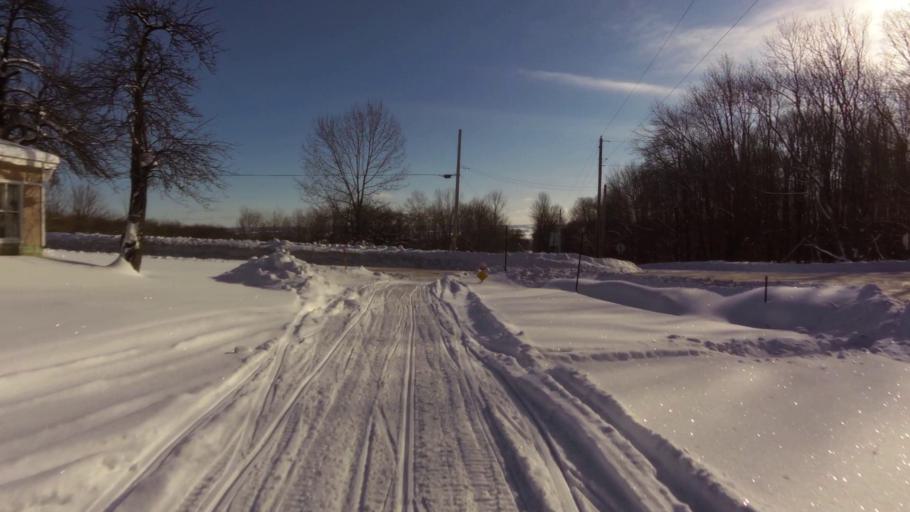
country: US
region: New York
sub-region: Chautauqua County
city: Falconer
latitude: 42.2605
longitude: -79.1128
